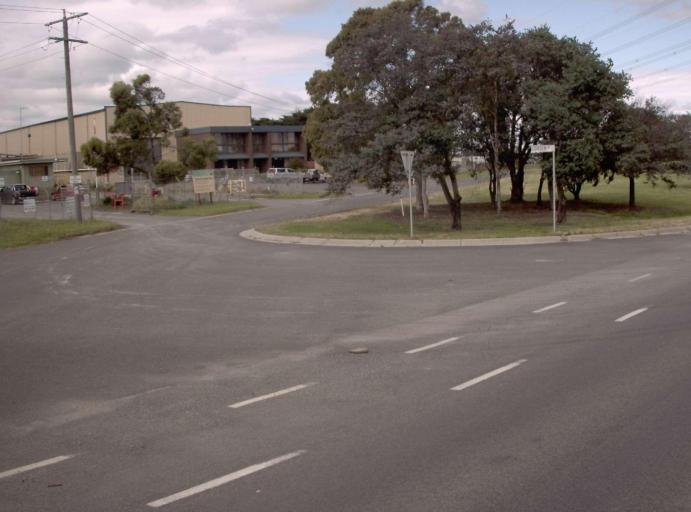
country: AU
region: Victoria
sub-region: Latrobe
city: Morwell
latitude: -38.2325
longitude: 146.4430
